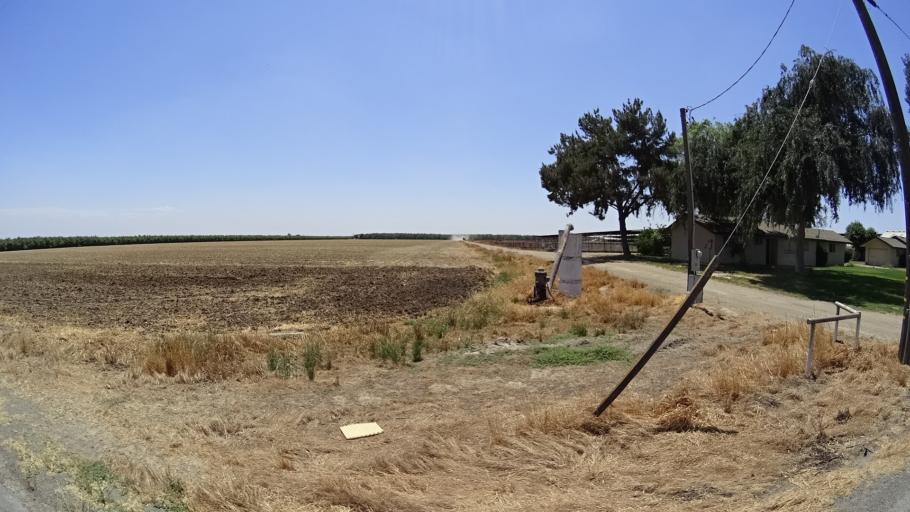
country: US
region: California
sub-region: Fresno County
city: Kingsburg
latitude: 36.4305
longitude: -119.5444
